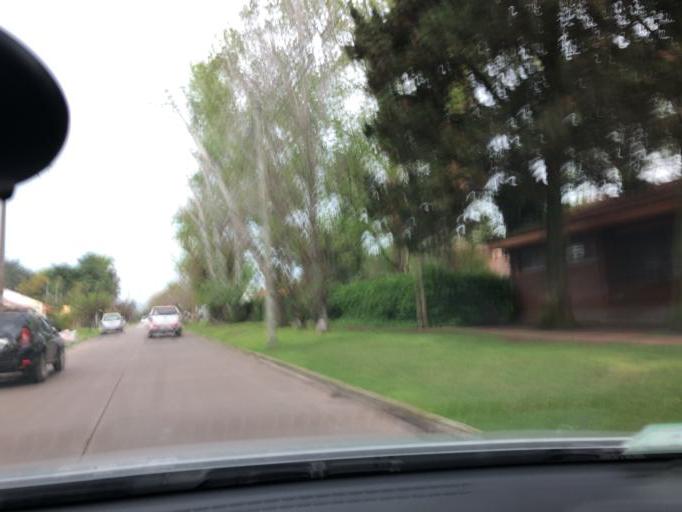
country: AR
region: Buenos Aires
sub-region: Partido de La Plata
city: La Plata
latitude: -34.8762
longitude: -58.0467
